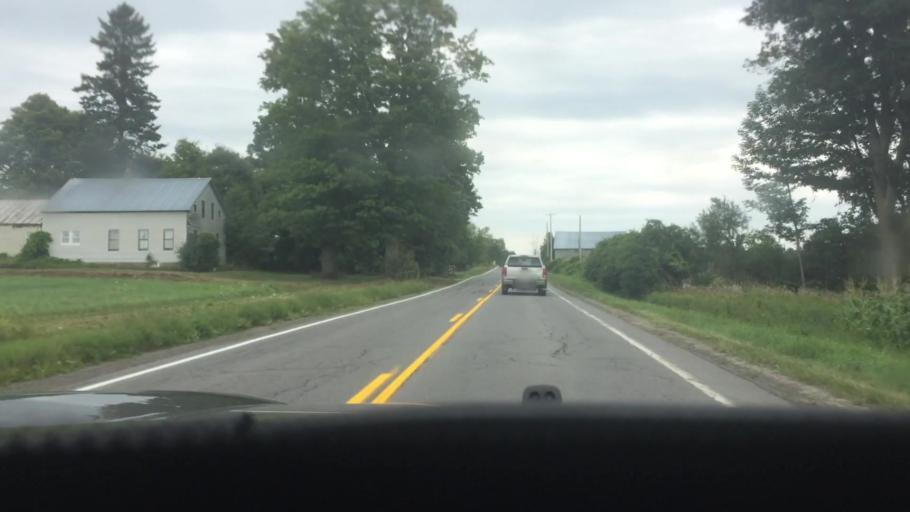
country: US
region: New York
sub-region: St. Lawrence County
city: Canton
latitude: 44.5432
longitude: -75.1571
